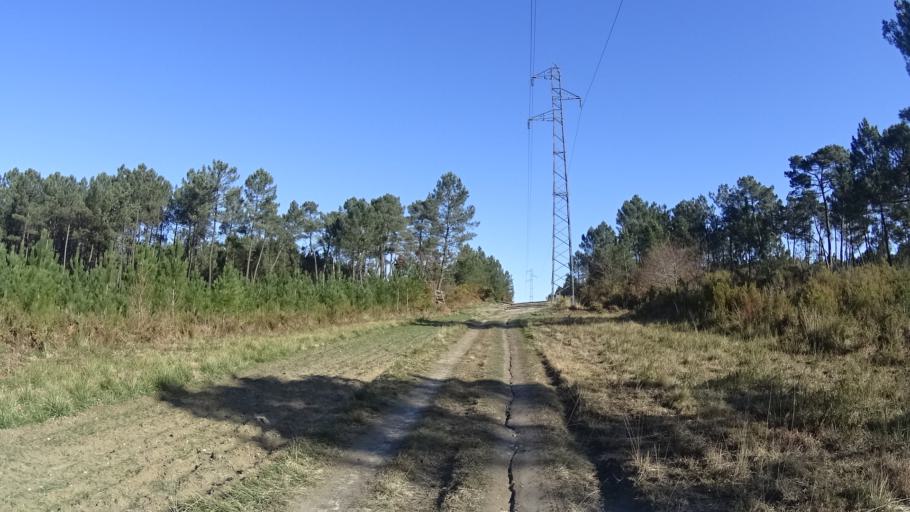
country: FR
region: Aquitaine
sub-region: Departement de la Dordogne
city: La Roche-Chalais
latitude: 45.1682
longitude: 0.0341
